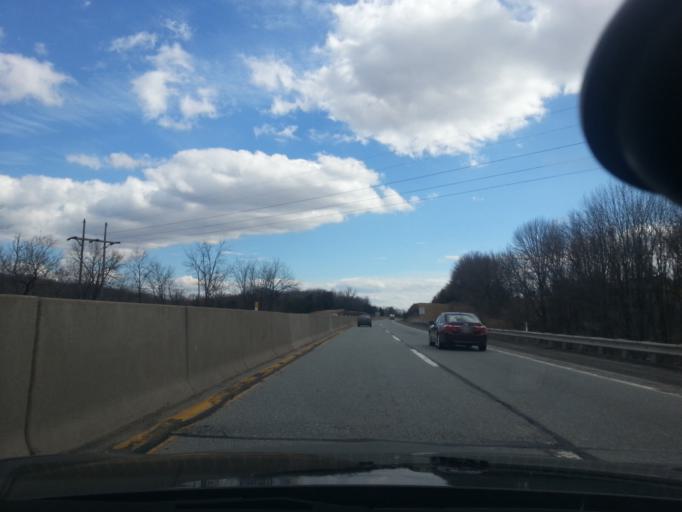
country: US
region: Pennsylvania
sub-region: Bucks County
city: Spinnerstown
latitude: 40.4295
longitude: -75.4199
